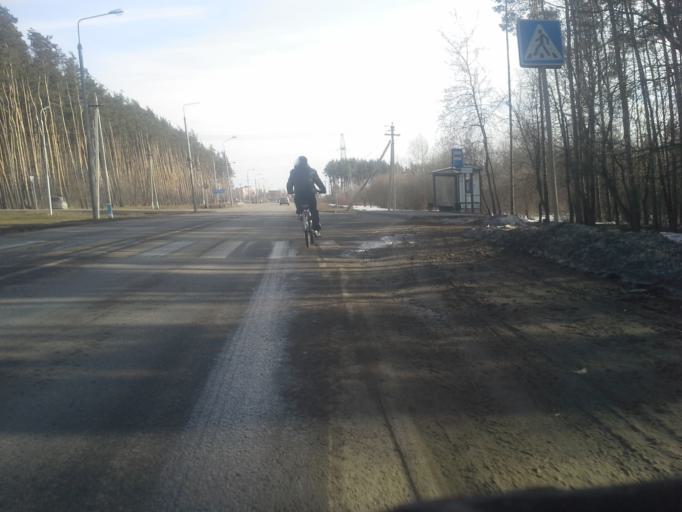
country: RU
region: Moskovskaya
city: Shcherbinka
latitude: 55.4833
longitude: 37.5202
